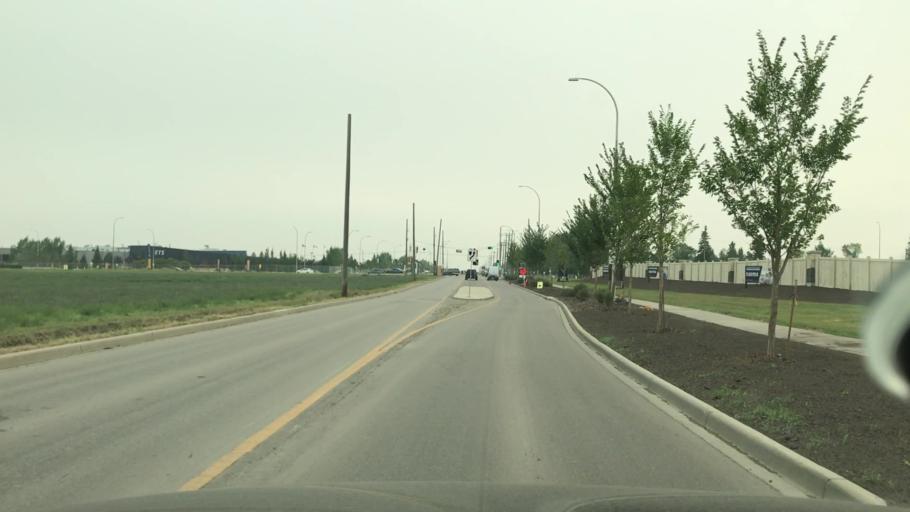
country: CA
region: Alberta
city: Devon
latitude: 53.4249
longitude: -113.5932
